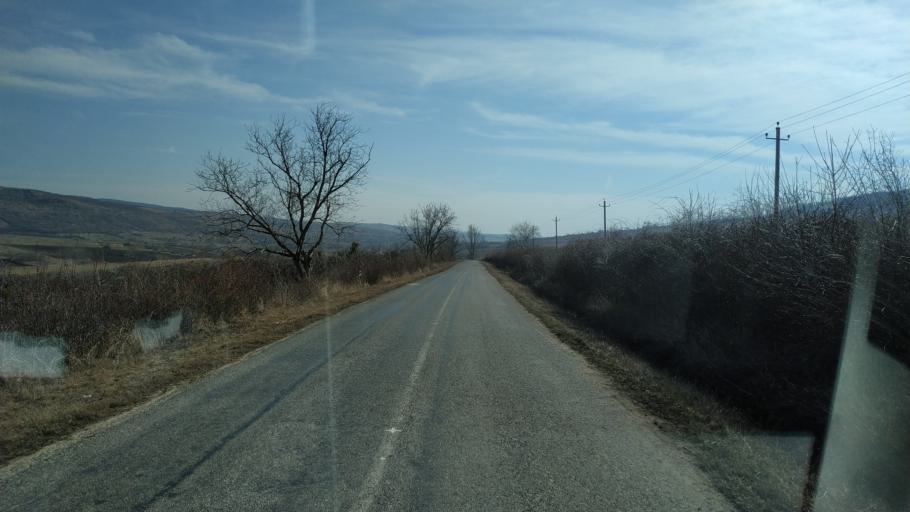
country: MD
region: Nisporeni
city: Nisporeni
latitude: 47.1760
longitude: 28.0858
